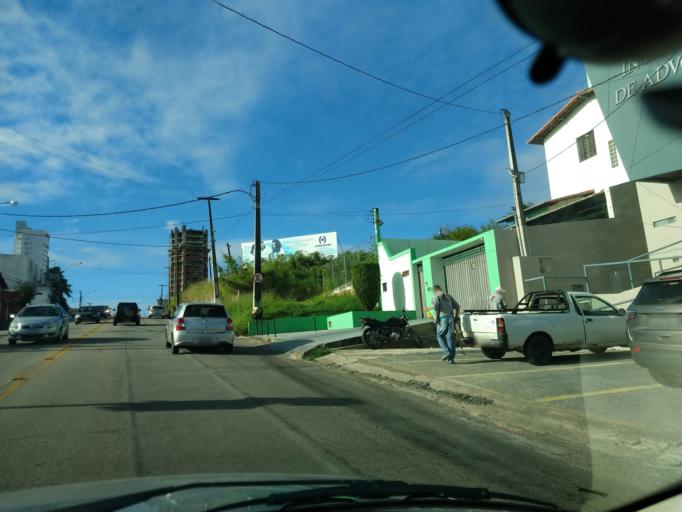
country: BR
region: Rio Grande do Norte
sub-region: Natal
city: Natal
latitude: -5.8315
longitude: -35.2229
